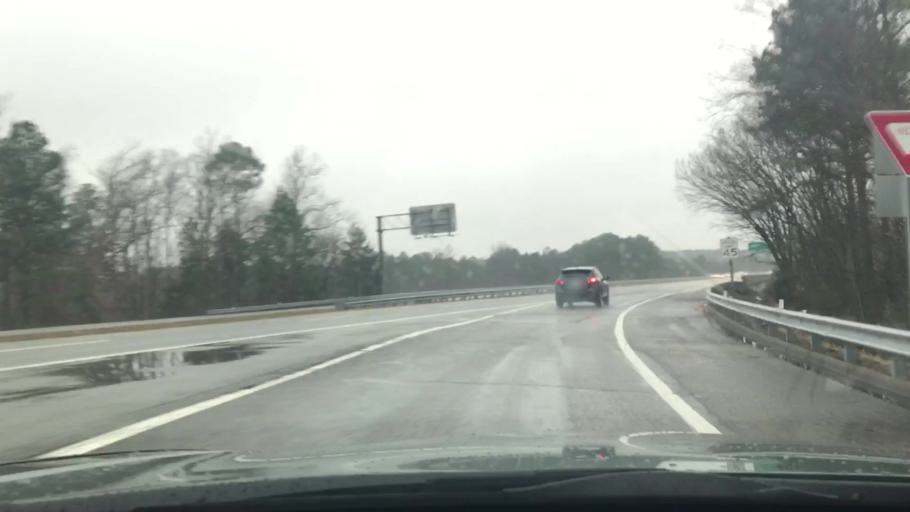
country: US
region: Virginia
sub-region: Henrico County
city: Short Pump
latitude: 37.6697
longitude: -77.5799
